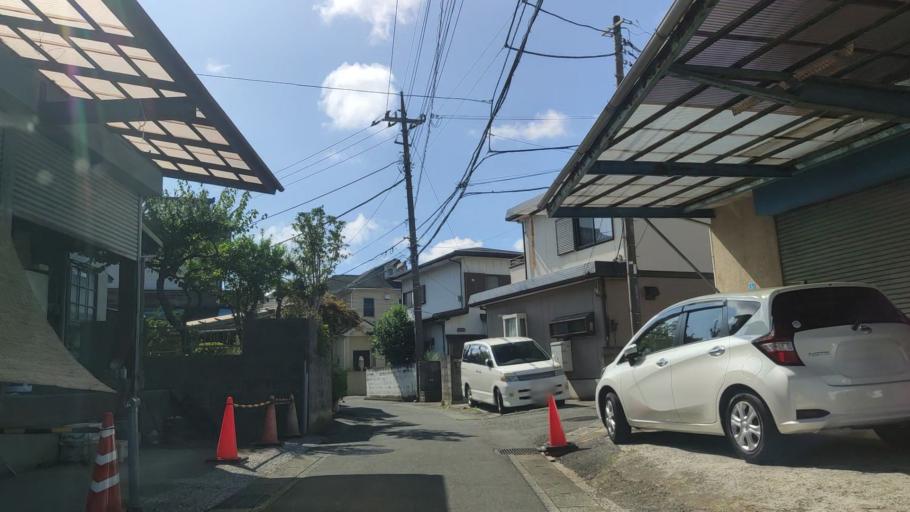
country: JP
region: Kanagawa
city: Yokohama
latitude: 35.4109
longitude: 139.5716
